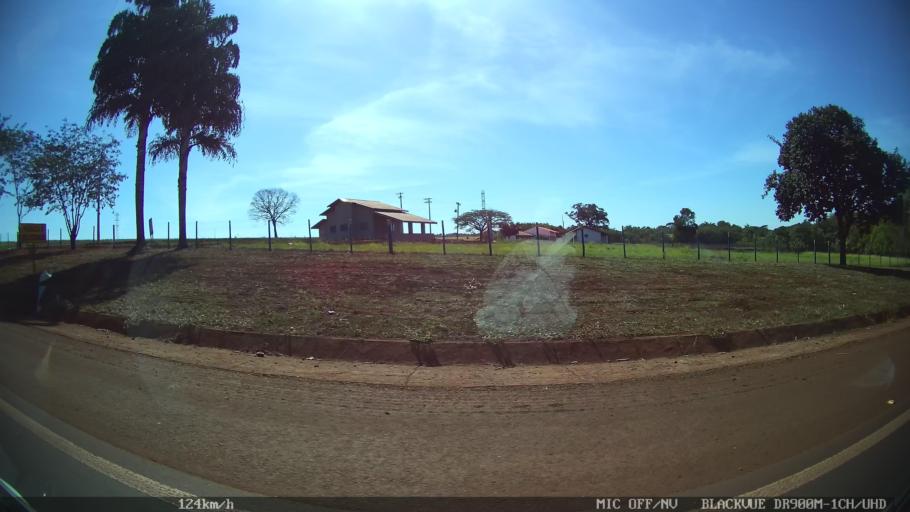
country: BR
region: Sao Paulo
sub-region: Guaira
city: Guaira
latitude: -20.4450
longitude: -48.3874
